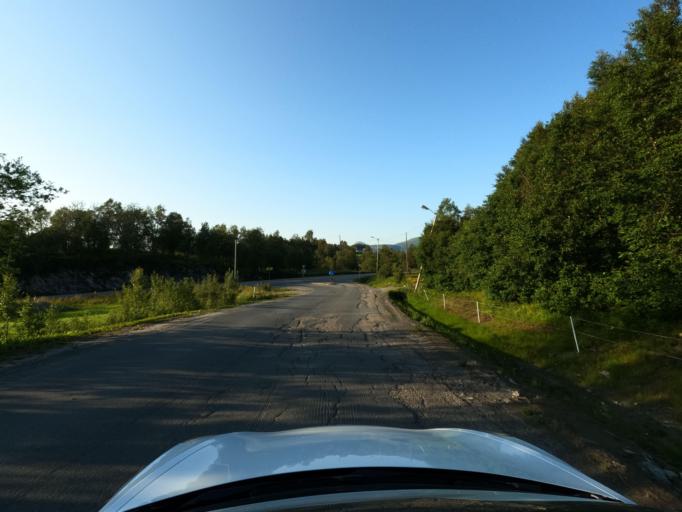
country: NO
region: Troms
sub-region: Skanland
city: Evenskjer
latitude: 68.4911
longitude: 16.7159
